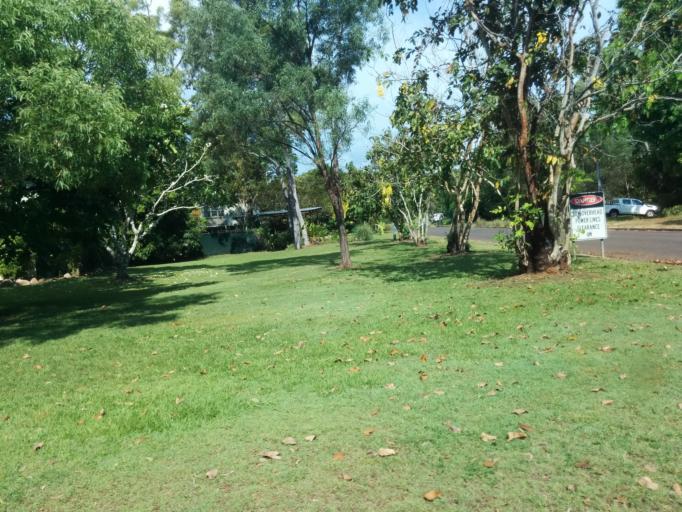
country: AU
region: Northern Territory
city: Alyangula
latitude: -13.8499
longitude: 136.4209
